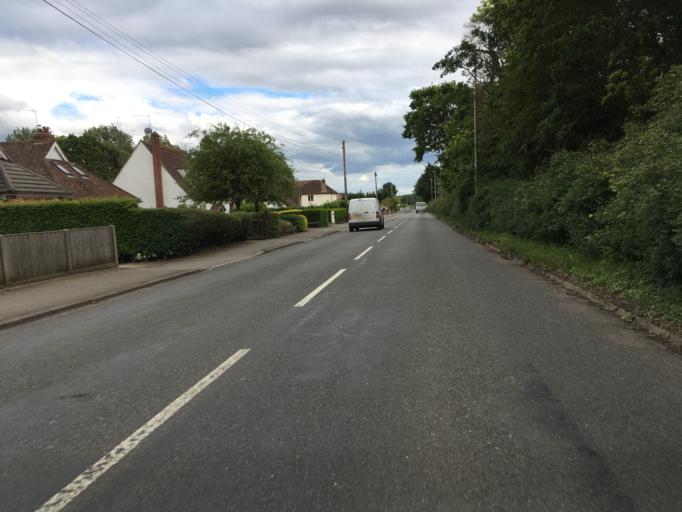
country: GB
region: England
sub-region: Oxfordshire
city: Boars Hill
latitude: 51.6938
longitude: -1.2971
